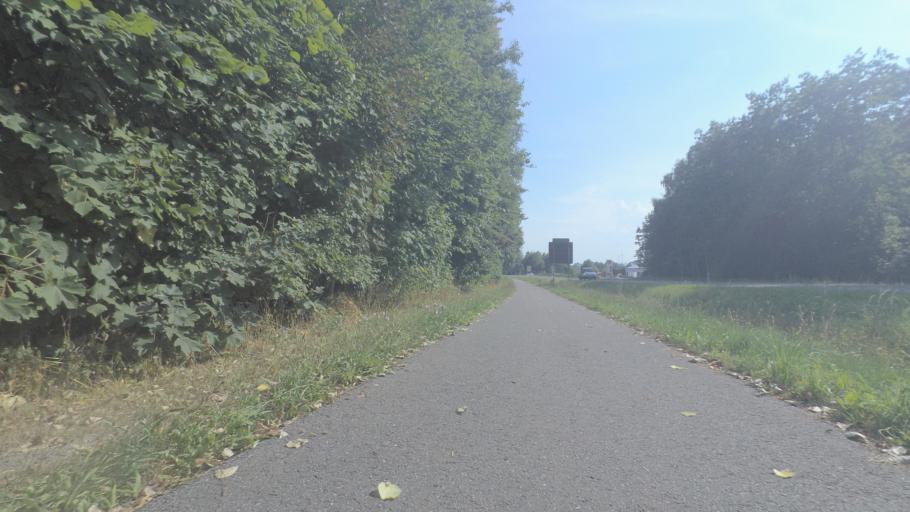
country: DE
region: Mecklenburg-Vorpommern
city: Grimmen
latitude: 54.1095
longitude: 13.0590
